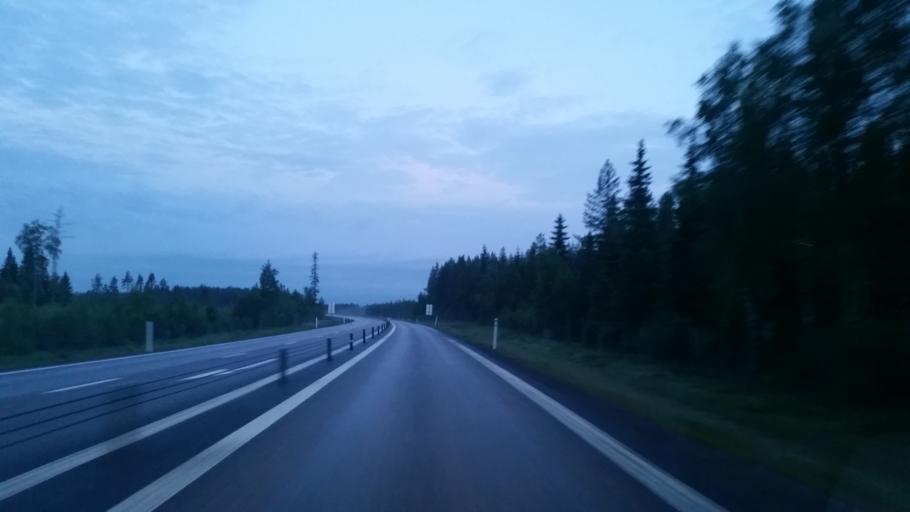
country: SE
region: Vaesterbotten
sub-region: Robertsfors Kommun
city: Robertsfors
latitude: 64.1250
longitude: 20.8847
